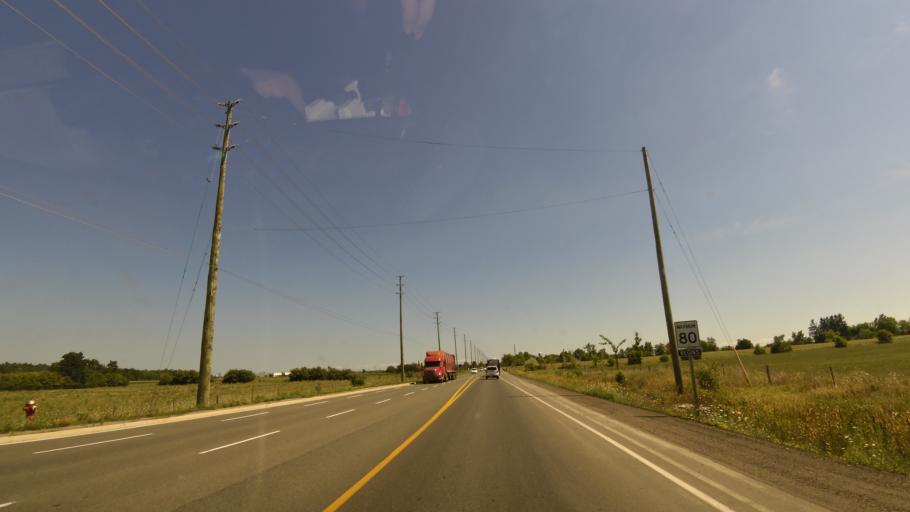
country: CA
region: Ontario
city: Brampton
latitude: 43.6268
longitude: -79.8240
